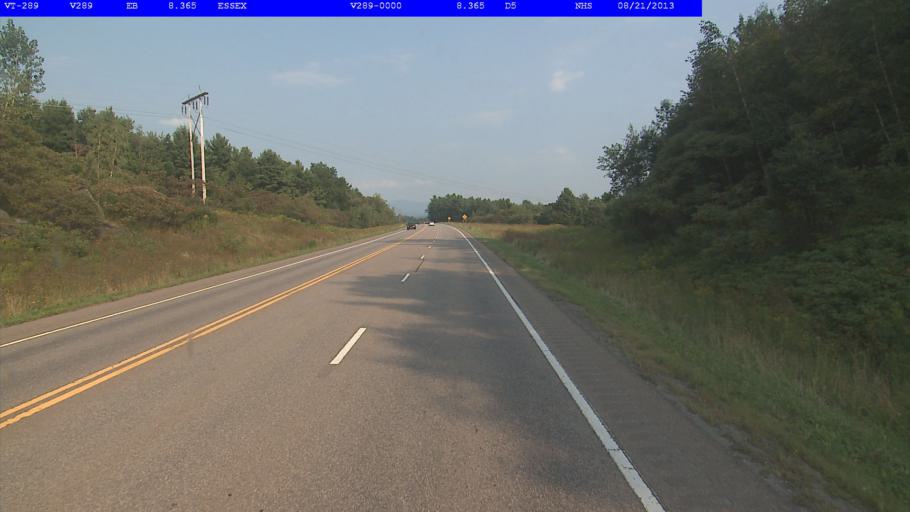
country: US
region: Vermont
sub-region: Chittenden County
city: Essex Junction
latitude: 44.5152
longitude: -73.1067
